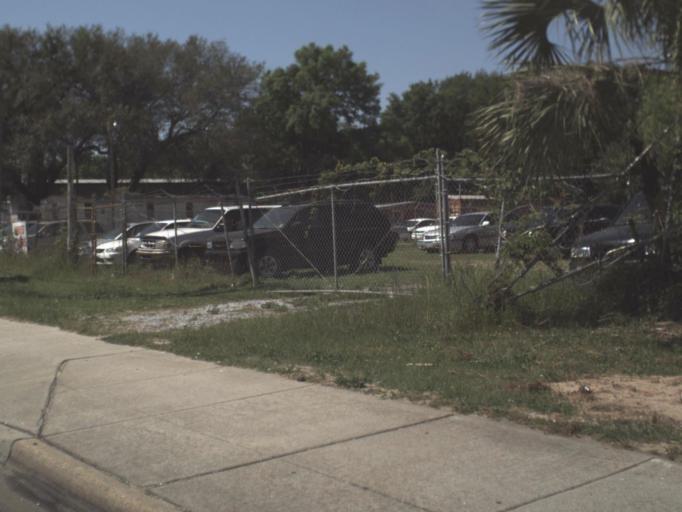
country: US
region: Florida
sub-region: Escambia County
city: Brent
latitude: 30.4523
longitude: -87.2398
